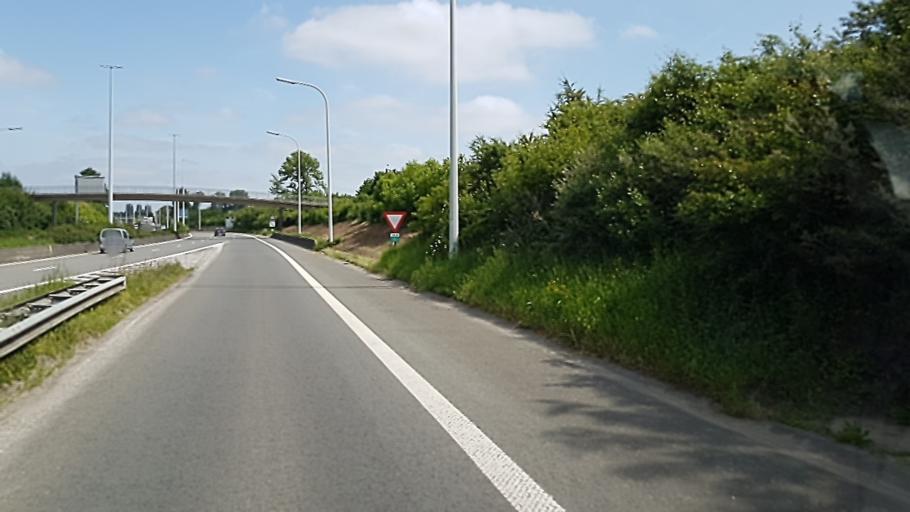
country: BE
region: Flanders
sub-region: Provincie West-Vlaanderen
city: Kortrijk
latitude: 50.8373
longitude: 3.2223
